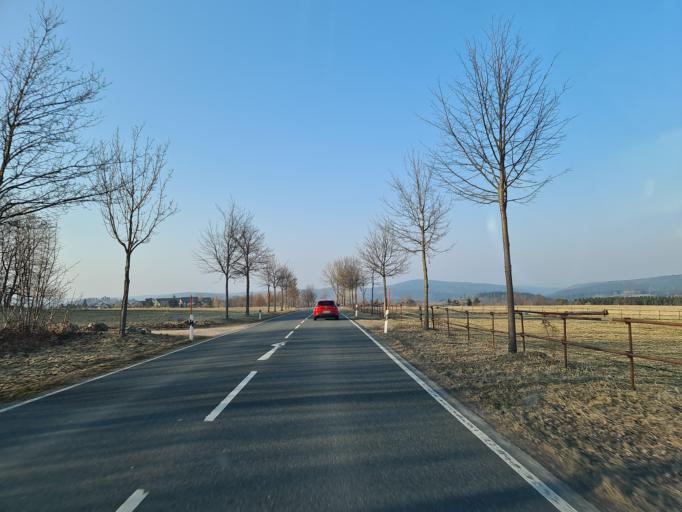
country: DE
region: Saxony
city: Eibenstock
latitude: 50.4826
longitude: 12.6089
